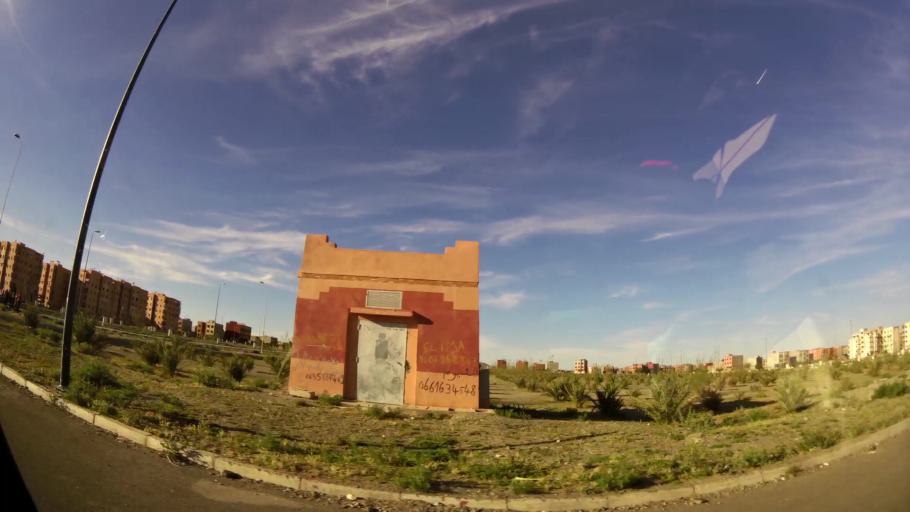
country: MA
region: Marrakech-Tensift-Al Haouz
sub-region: Marrakech
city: Marrakesh
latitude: 31.7636
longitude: -8.1068
